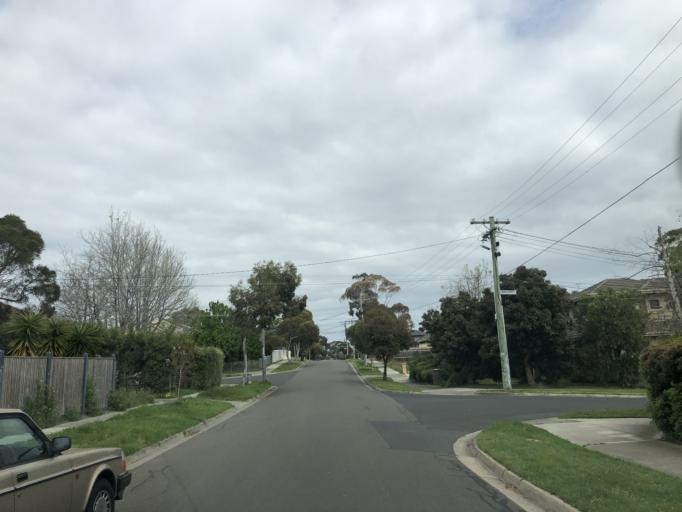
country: AU
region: Victoria
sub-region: Monash
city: Ashwood
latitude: -37.8696
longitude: 145.1052
